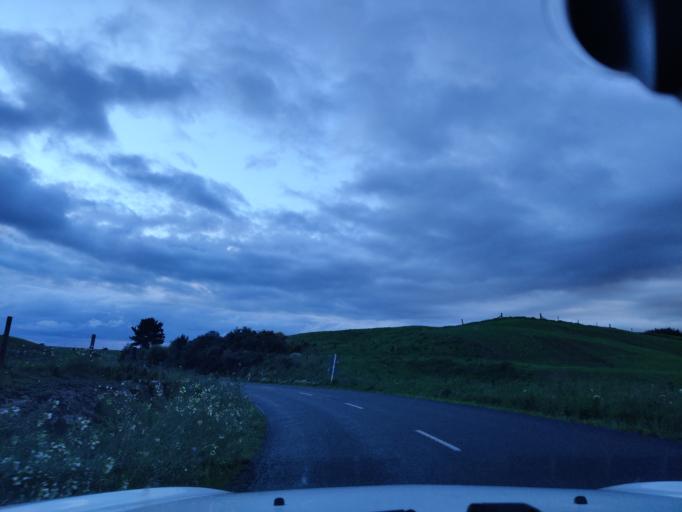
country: NZ
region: Waikato
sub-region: South Waikato District
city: Tokoroa
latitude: -38.1783
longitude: 175.7787
